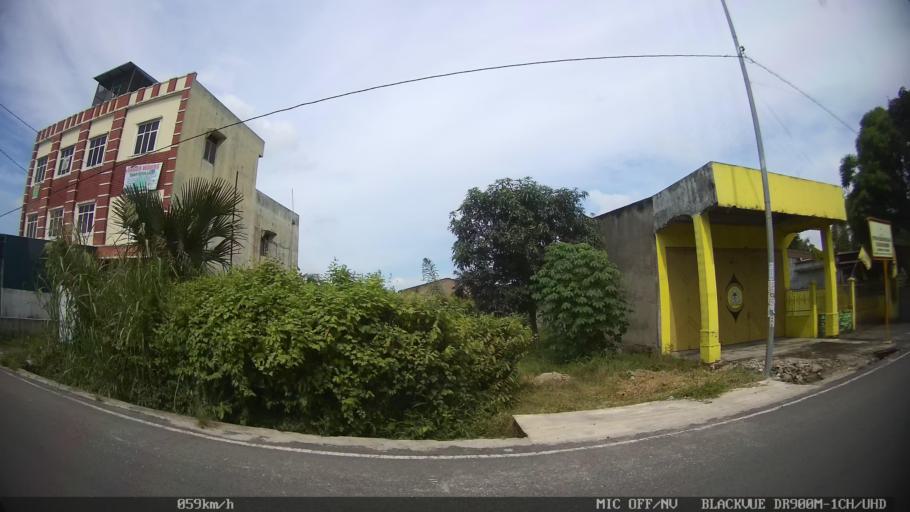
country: ID
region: North Sumatra
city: Percut
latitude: 3.5902
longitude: 98.8589
